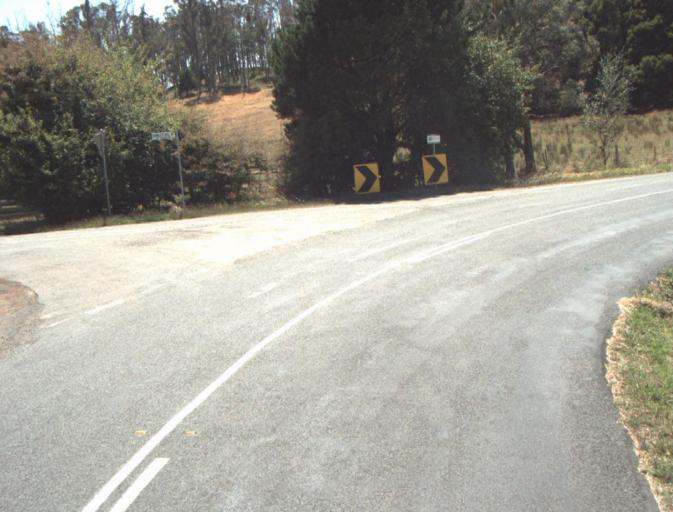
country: AU
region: Tasmania
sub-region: Launceston
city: Mayfield
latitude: -41.2592
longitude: 147.1361
